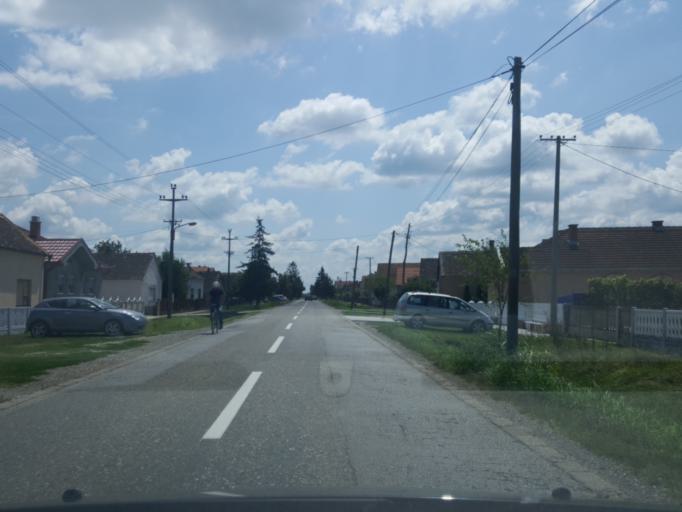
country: RS
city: Glusci
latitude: 44.8869
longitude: 19.5512
